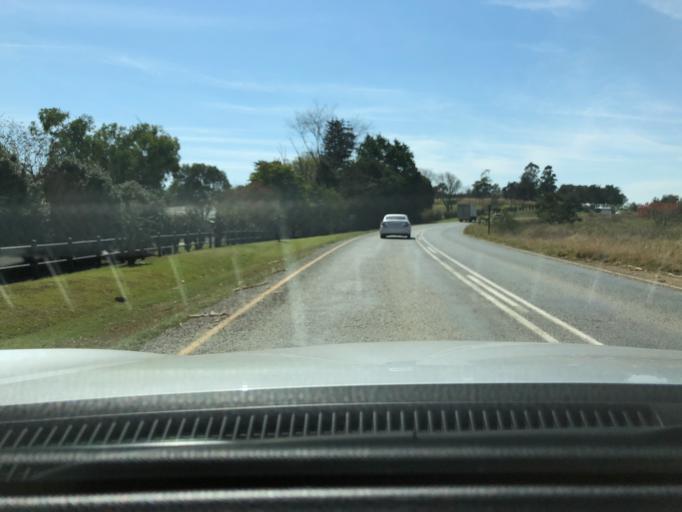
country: ZA
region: KwaZulu-Natal
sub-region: uMgungundlovu District Municipality
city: Camperdown
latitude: -29.7418
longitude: 30.4210
